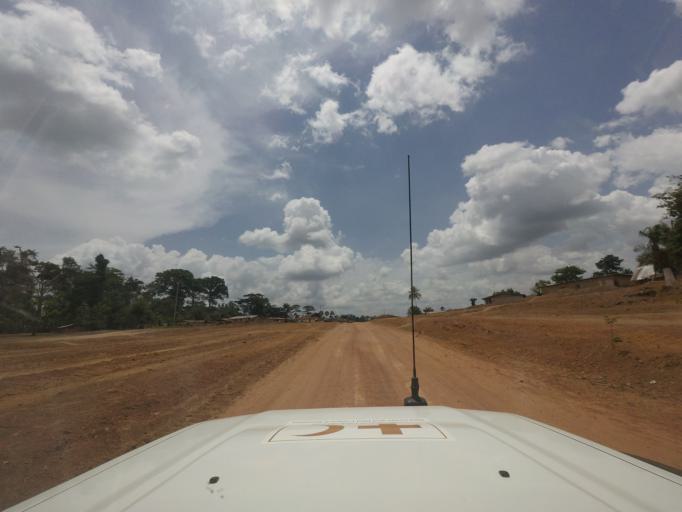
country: LR
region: Nimba
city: Sanniquellie
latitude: 7.2311
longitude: -8.8909
